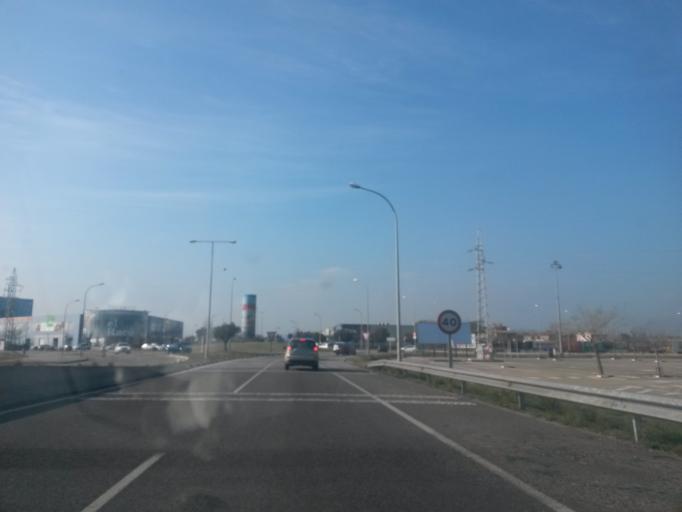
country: ES
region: Catalonia
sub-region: Provincia de Girona
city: Vila-sacra
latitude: 42.2676
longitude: 3.0003
